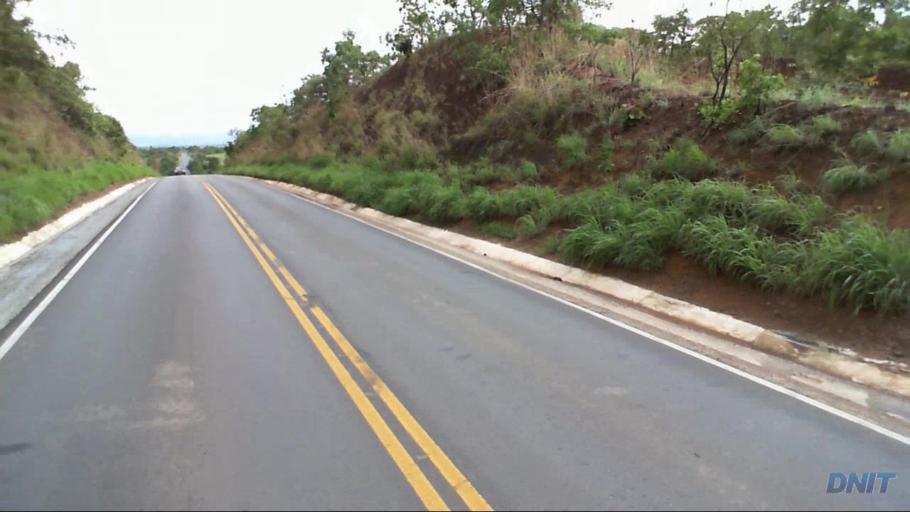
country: BR
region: Goias
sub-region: Padre Bernardo
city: Padre Bernardo
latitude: -15.2181
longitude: -48.2806
